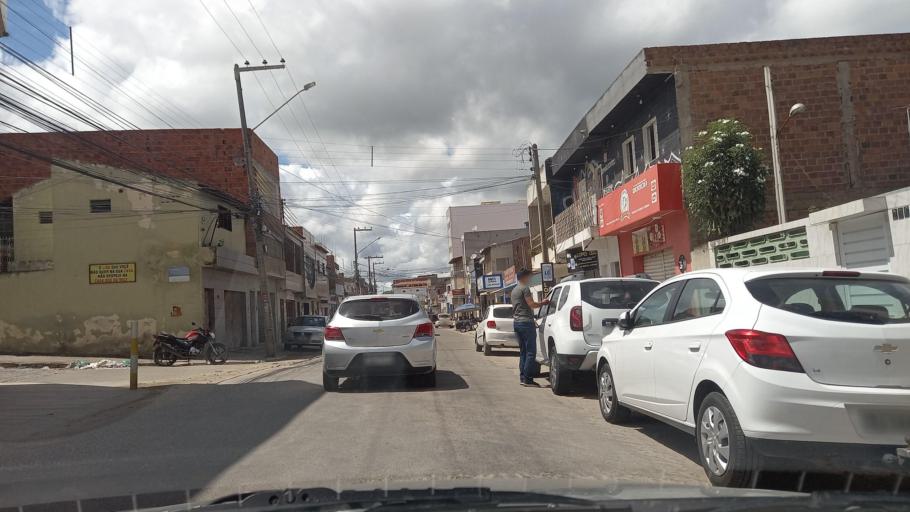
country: BR
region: Pernambuco
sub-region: Caruaru
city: Caruaru
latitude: -8.2828
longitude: -35.9587
